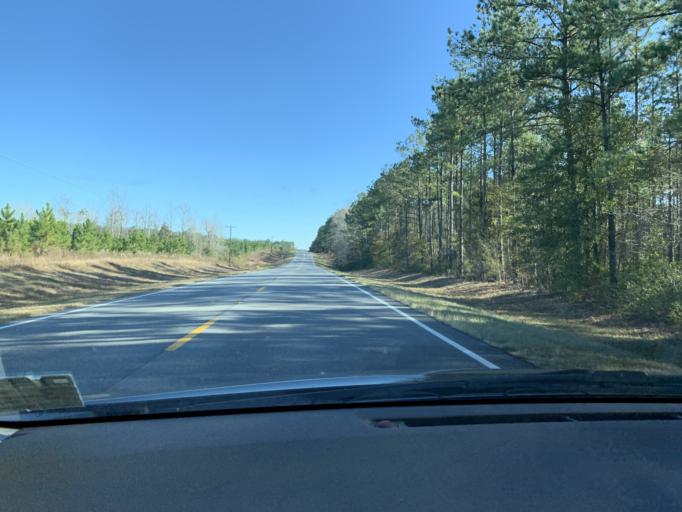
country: US
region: Georgia
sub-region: Ben Hill County
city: Fitzgerald
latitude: 31.7613
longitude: -83.1169
